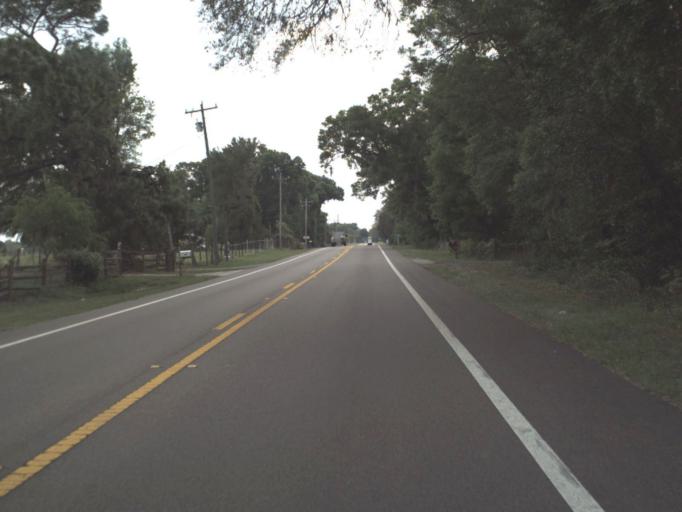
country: US
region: Florida
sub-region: Lake County
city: Umatilla
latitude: 28.9858
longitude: -81.6440
